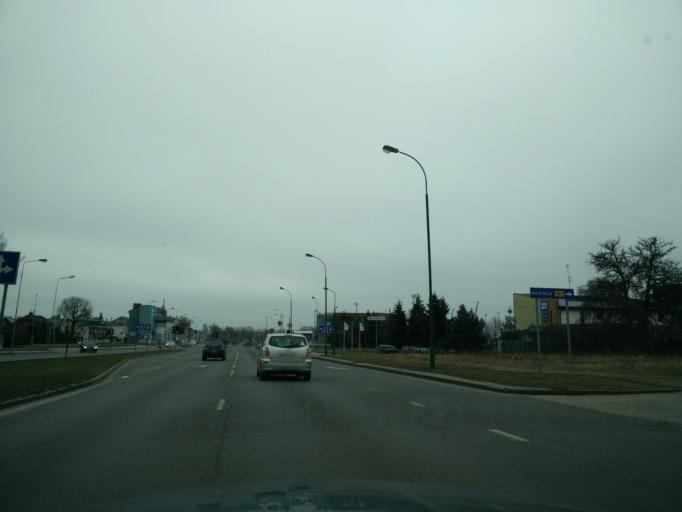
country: LT
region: Klaipedos apskritis
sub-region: Klaipeda
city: Klaipeda
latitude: 55.6903
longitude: 21.1439
